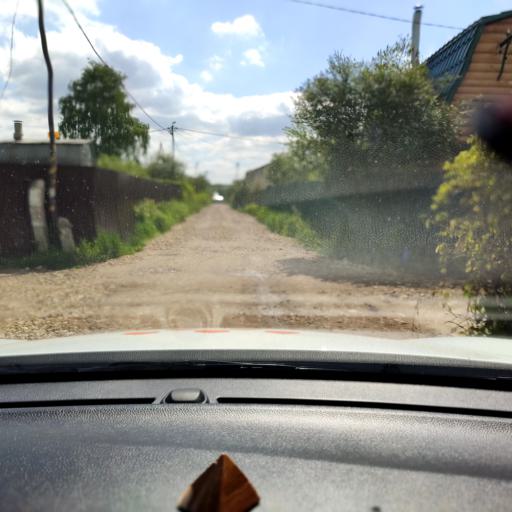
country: RU
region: Tatarstan
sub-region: Gorod Kazan'
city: Kazan
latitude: 55.8613
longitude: 49.1852
